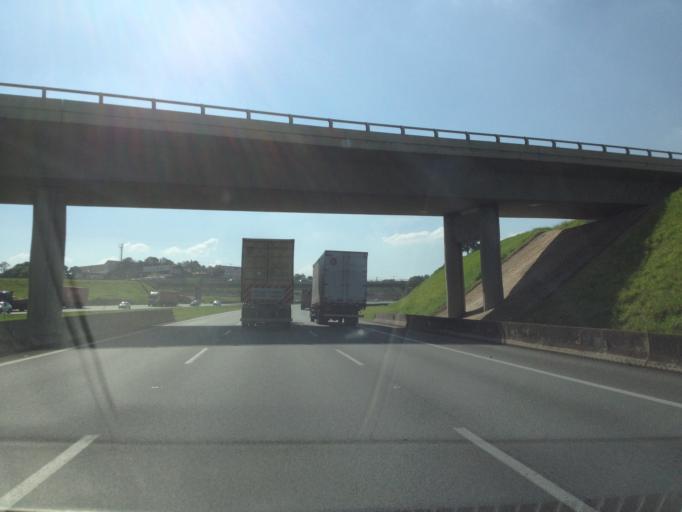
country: BR
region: Sao Paulo
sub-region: Campinas
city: Campinas
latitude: -22.9938
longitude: -47.1082
